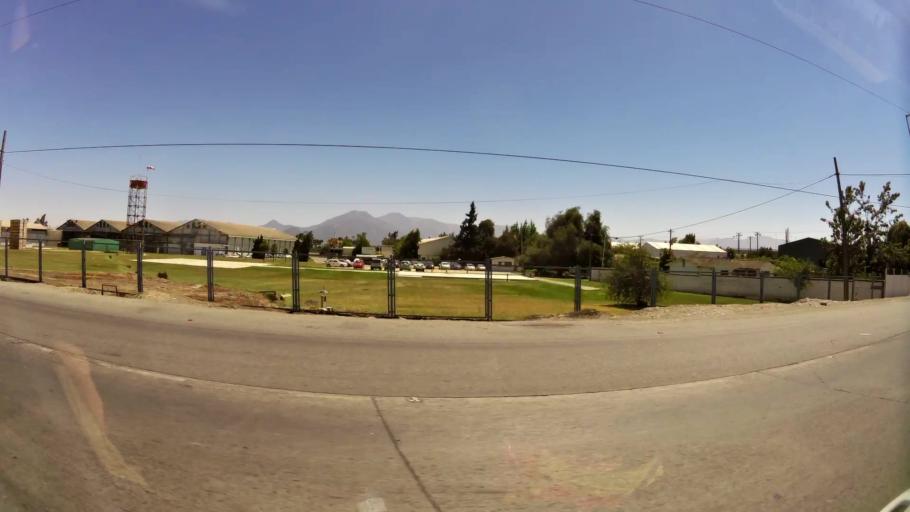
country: CL
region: O'Higgins
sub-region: Provincia de Cachapoal
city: Rancagua
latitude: -34.2122
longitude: -70.7698
